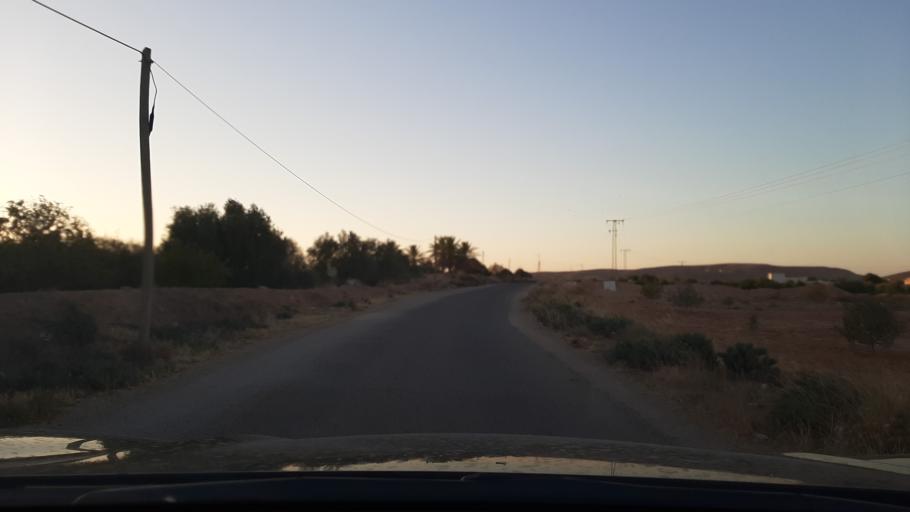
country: TN
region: Qabis
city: Matmata
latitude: 33.5577
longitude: 10.1841
